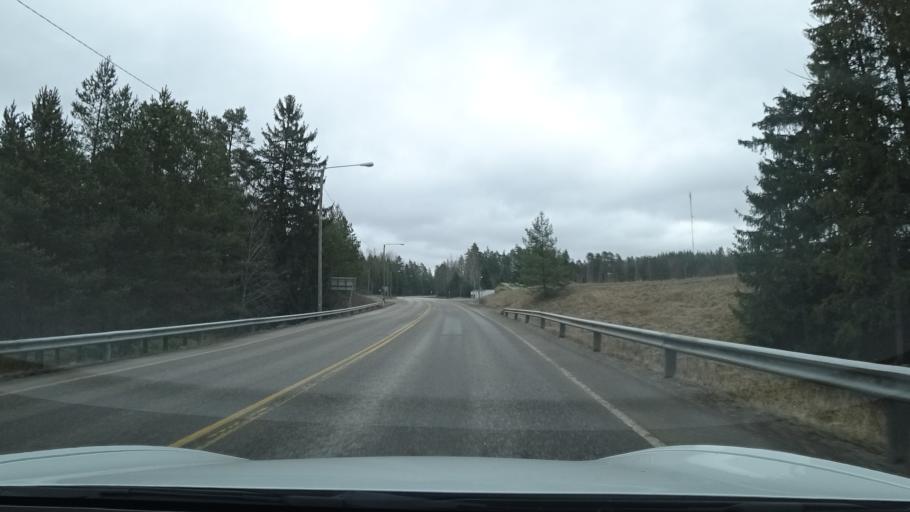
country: FI
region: Uusimaa
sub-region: Porvoo
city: Pukkila
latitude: 60.6403
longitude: 25.5910
